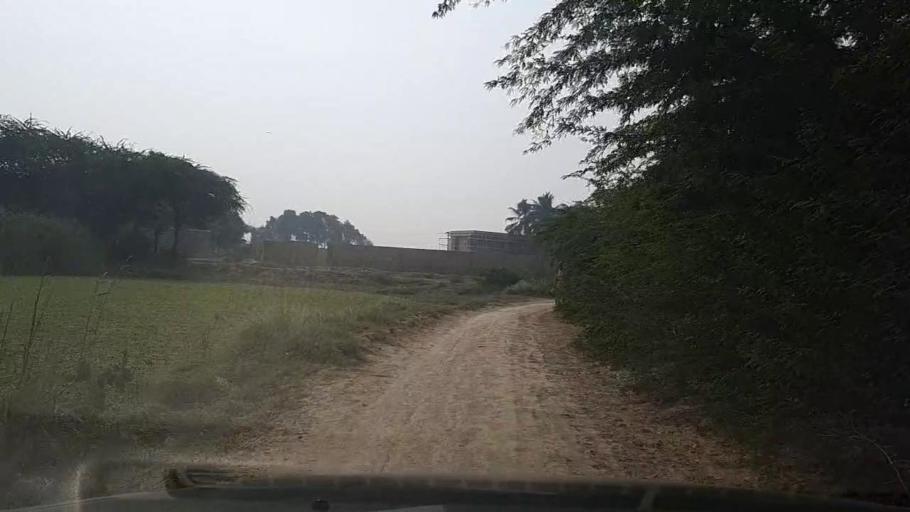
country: PK
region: Sindh
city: Mirpur Sakro
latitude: 24.5523
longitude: 67.8395
